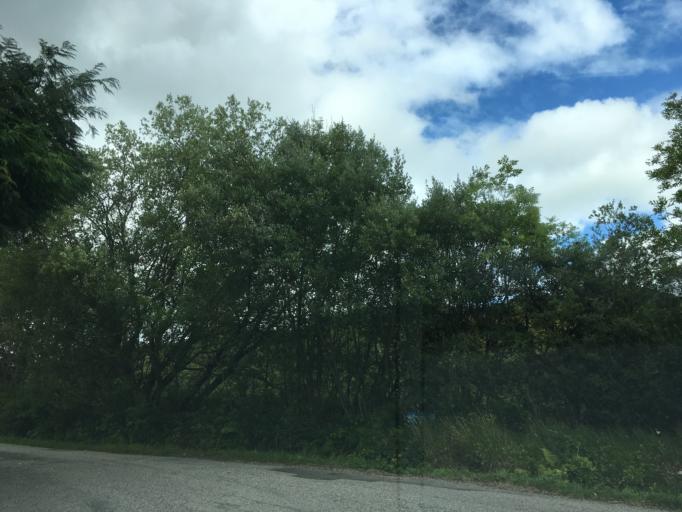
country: GB
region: Scotland
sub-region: Argyll and Bute
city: Oban
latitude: 56.3510
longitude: -5.1765
